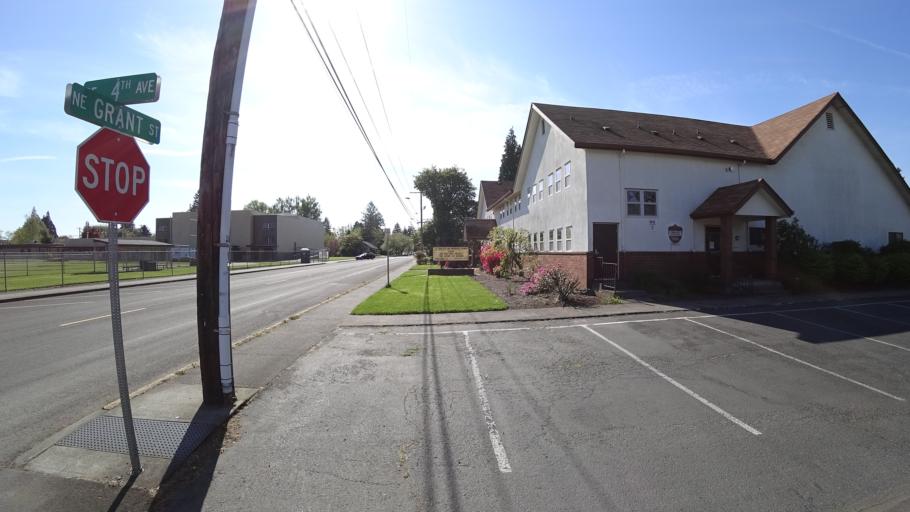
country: US
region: Oregon
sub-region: Washington County
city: Hillsboro
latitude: 45.5284
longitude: -122.9845
